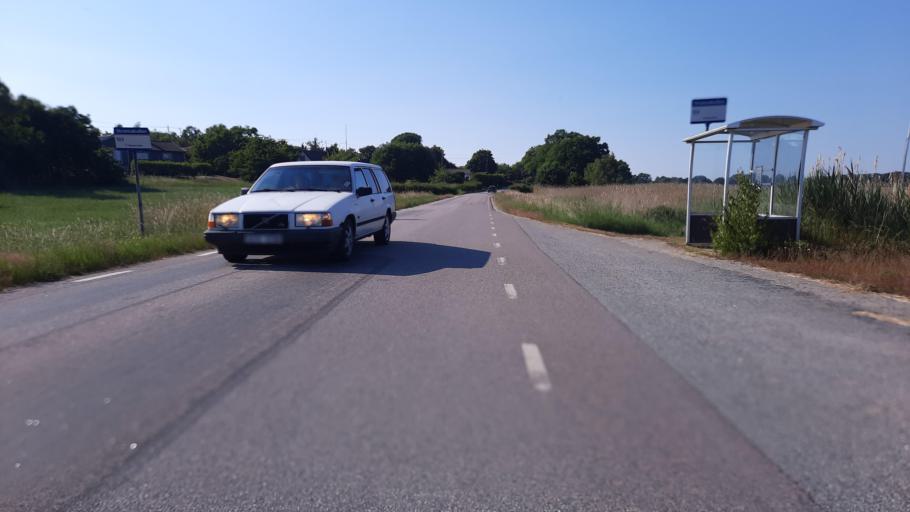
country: SE
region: Blekinge
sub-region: Karlskrona Kommun
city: Sturko
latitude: 56.0993
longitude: 15.6931
